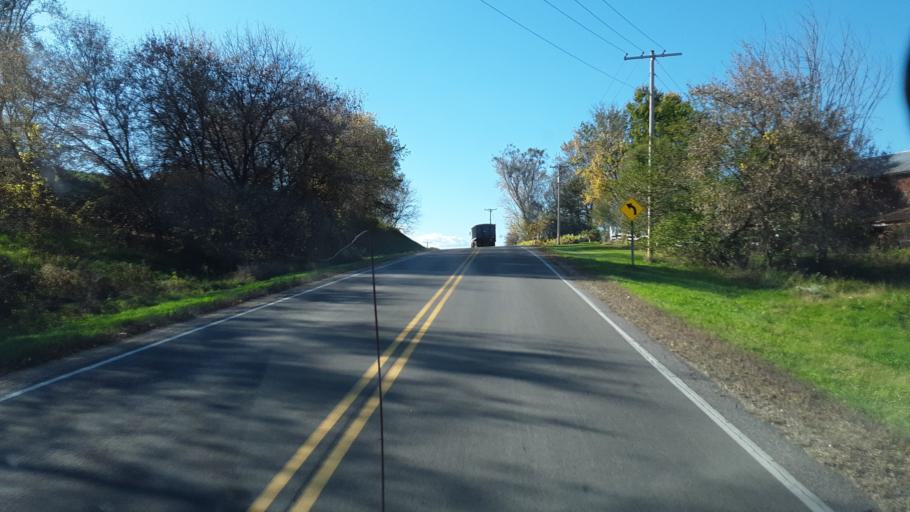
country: US
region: Wisconsin
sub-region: Sauk County
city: Reedsburg
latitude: 43.5407
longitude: -90.1457
